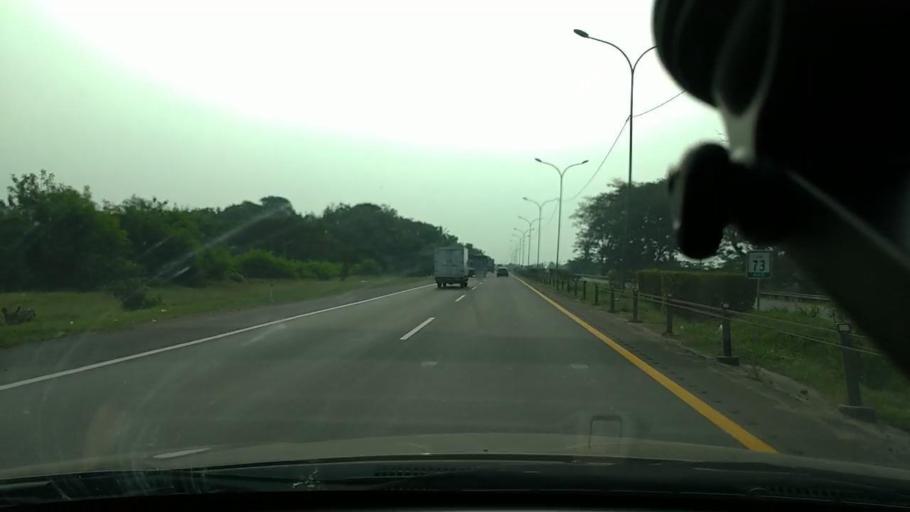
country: ID
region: Banten
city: Serang
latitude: -6.1054
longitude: 106.1765
